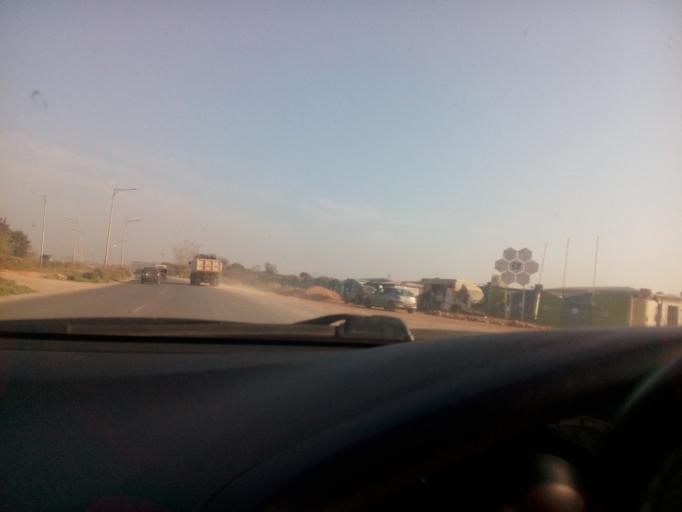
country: DZ
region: Oran
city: Es Senia
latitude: 35.6504
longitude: -0.6747
